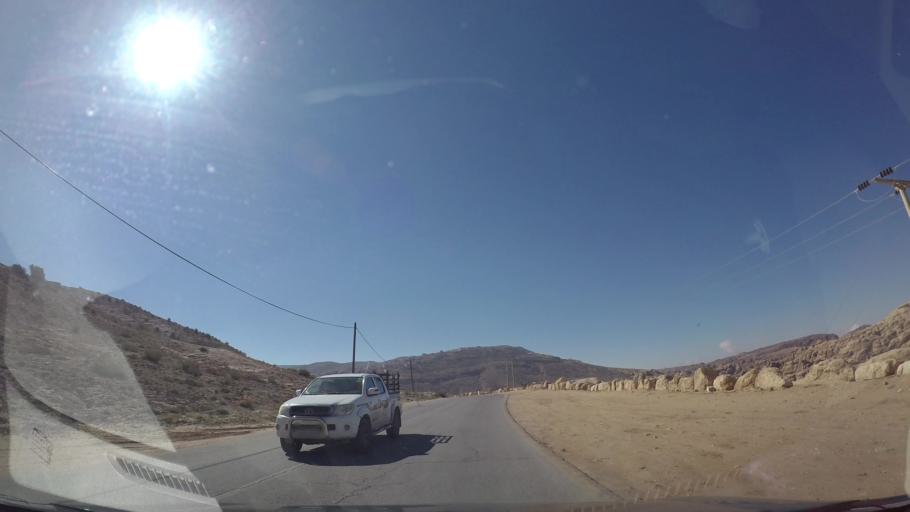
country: JO
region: Ma'an
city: Petra
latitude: 30.3330
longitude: 35.4679
